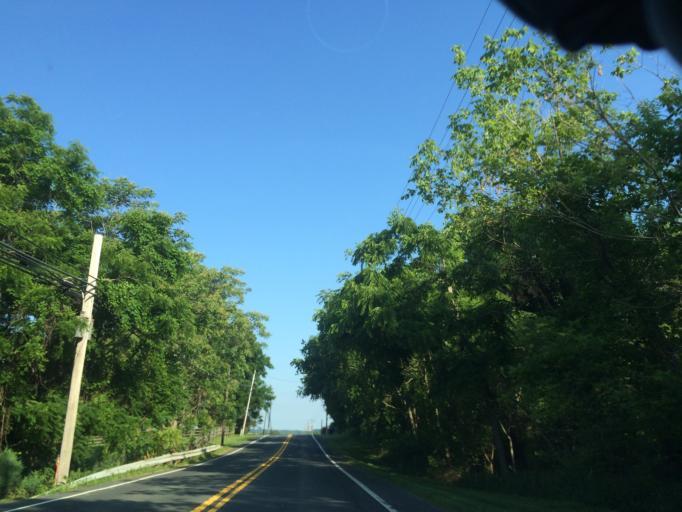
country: US
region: Maryland
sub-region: Carroll County
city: Sykesville
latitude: 39.3268
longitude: -77.0350
